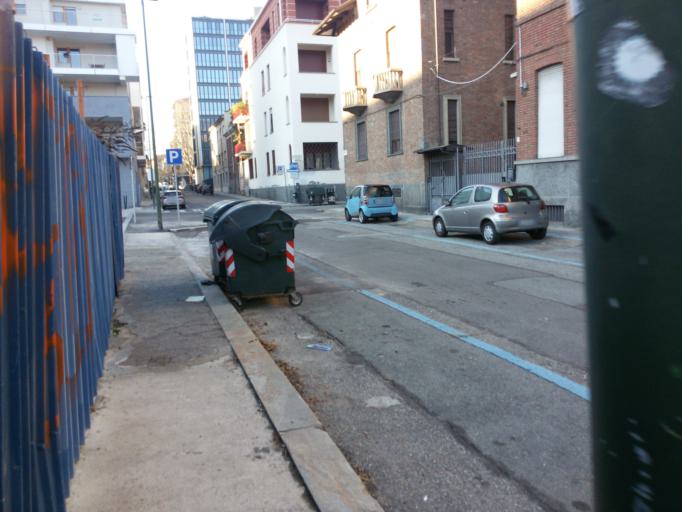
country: IT
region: Piedmont
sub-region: Provincia di Torino
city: Turin
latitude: 45.0469
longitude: 7.6813
